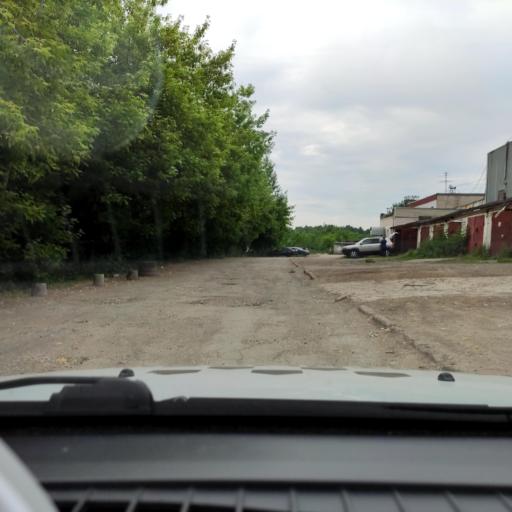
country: RU
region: Perm
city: Perm
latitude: 57.9742
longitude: 56.2876
